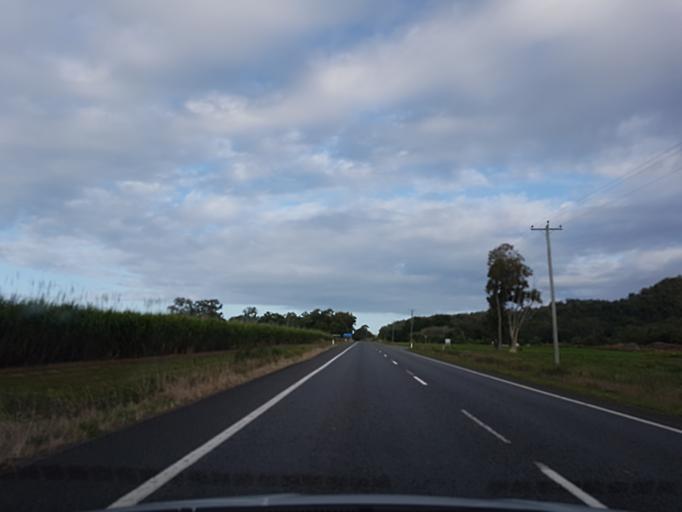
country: AU
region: Queensland
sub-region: Cairns
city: Port Douglas
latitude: -16.5575
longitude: 145.4902
